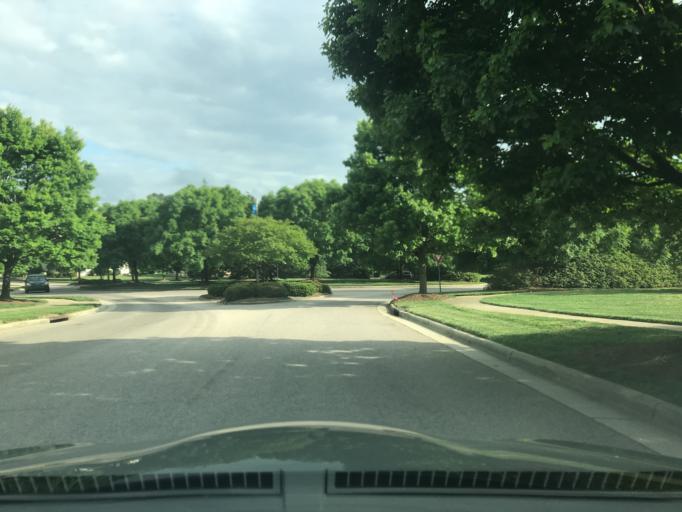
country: US
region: North Carolina
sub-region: Wake County
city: Wake Forest
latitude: 35.9186
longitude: -78.5702
